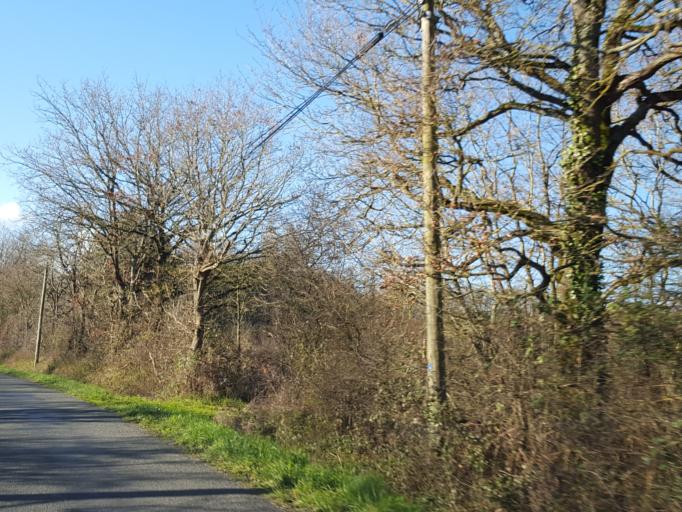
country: FR
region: Pays de la Loire
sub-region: Departement de la Vendee
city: Venansault
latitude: 46.6822
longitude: -1.4961
